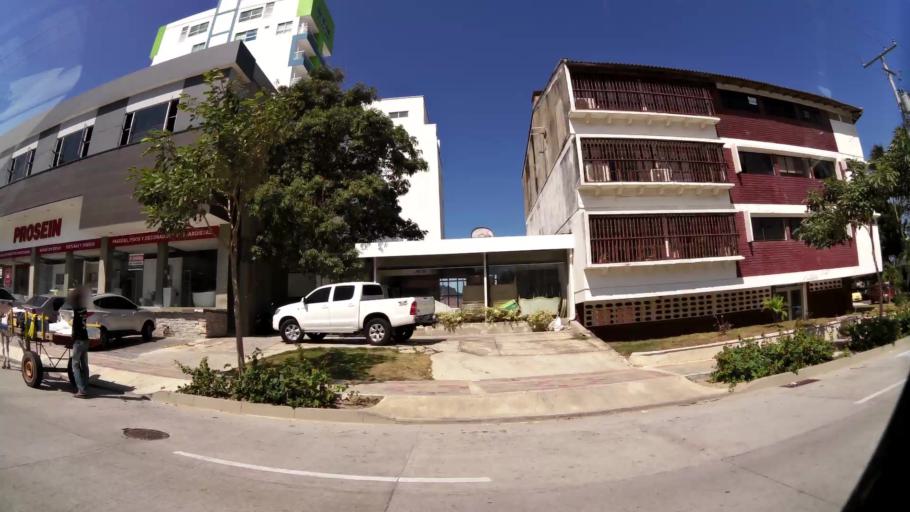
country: CO
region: Atlantico
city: Barranquilla
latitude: 11.0130
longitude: -74.8101
